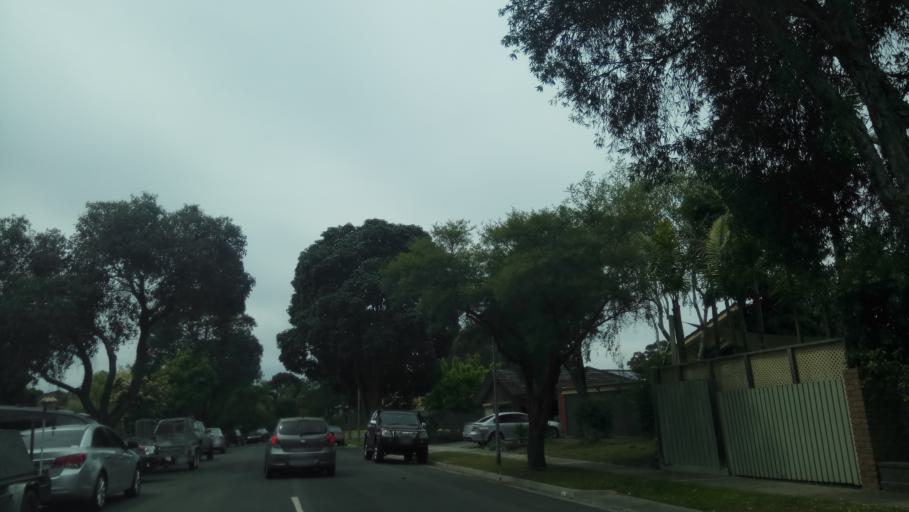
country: AU
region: Victoria
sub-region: Kingston
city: Dingley Village
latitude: -37.9745
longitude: 145.1294
